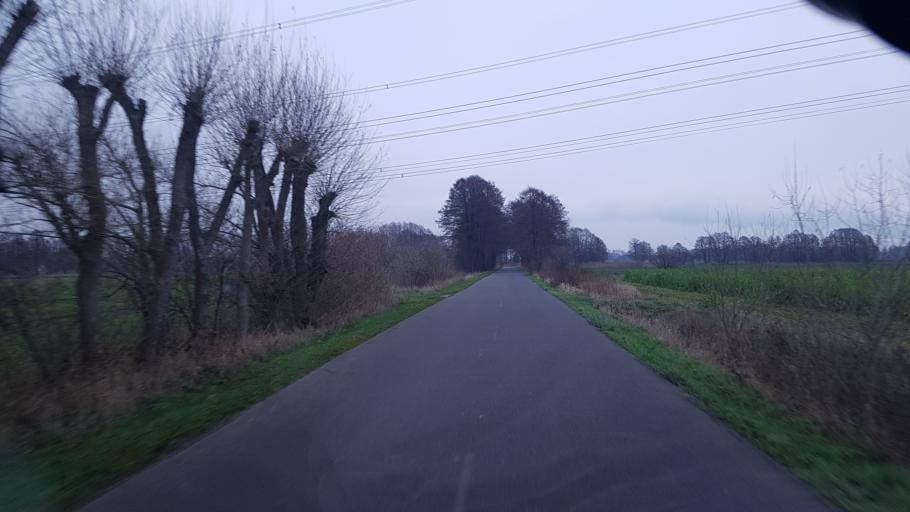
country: DE
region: Brandenburg
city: Peitz
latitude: 51.8844
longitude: 14.4057
